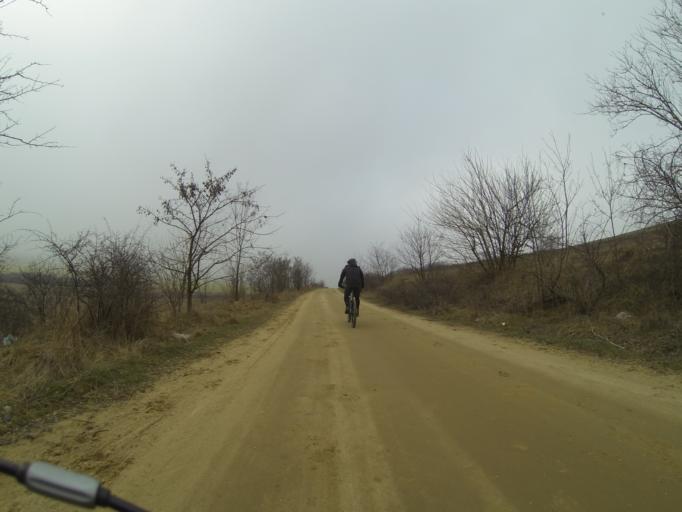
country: RO
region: Mehedinti
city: Padina Mica
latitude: 44.4810
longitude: 23.0392
